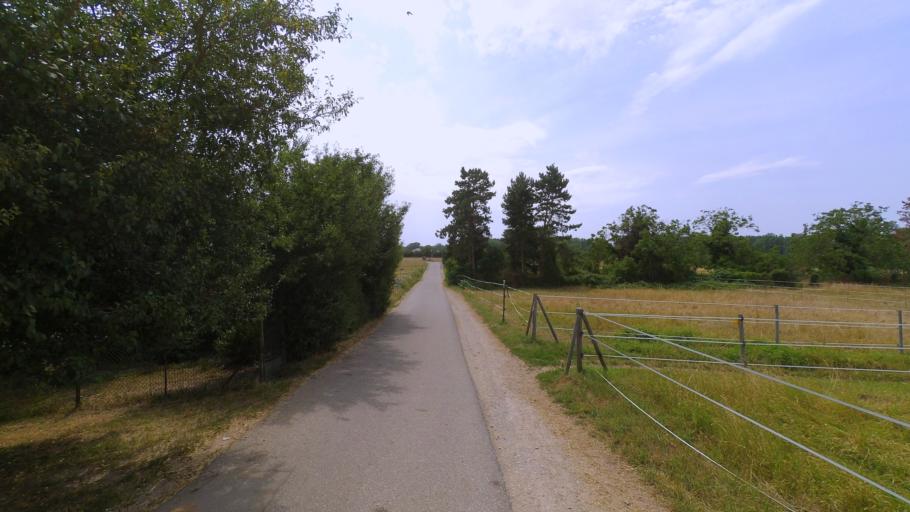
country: DE
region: Baden-Wuerttemberg
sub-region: Karlsruhe Region
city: Ketsch
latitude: 49.3812
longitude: 8.5335
